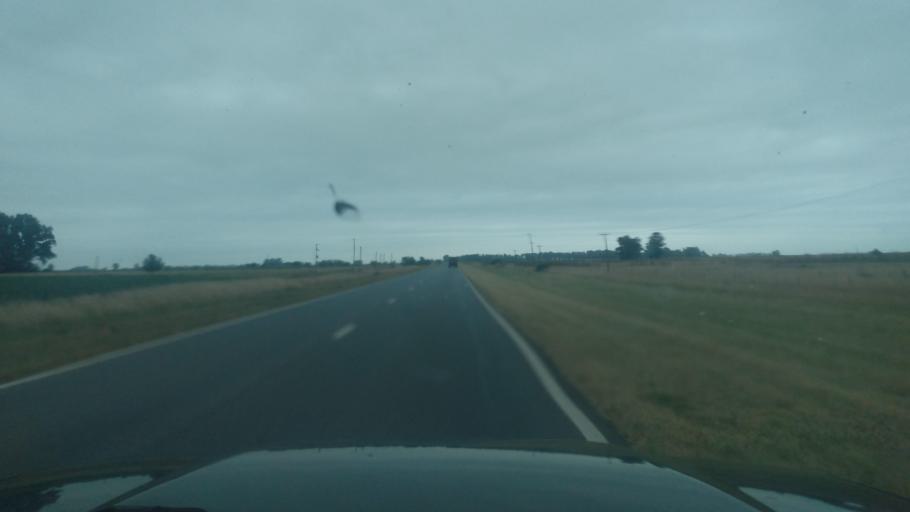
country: AR
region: Buenos Aires
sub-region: Partido de Nueve de Julio
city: Nueve de Julio
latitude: -35.4198
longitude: -60.7872
